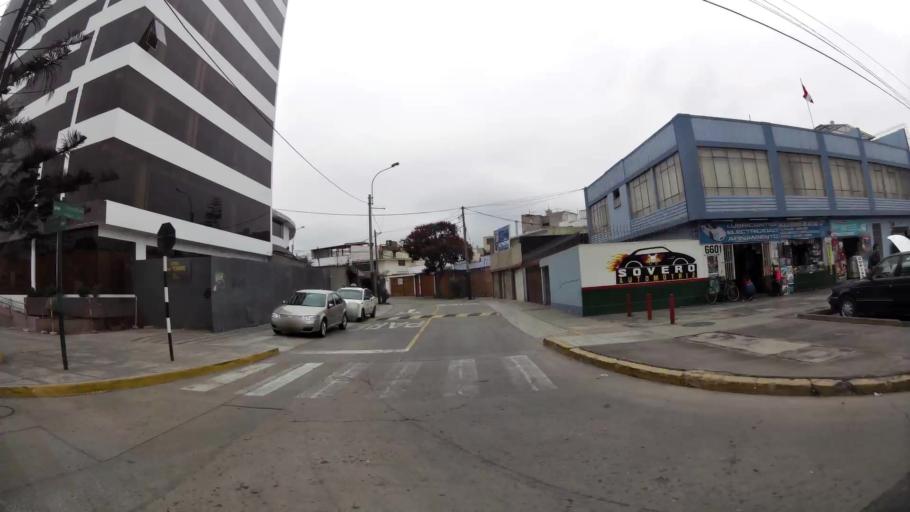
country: PE
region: Lima
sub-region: Lima
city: Surco
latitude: -12.1322
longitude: -77.0179
